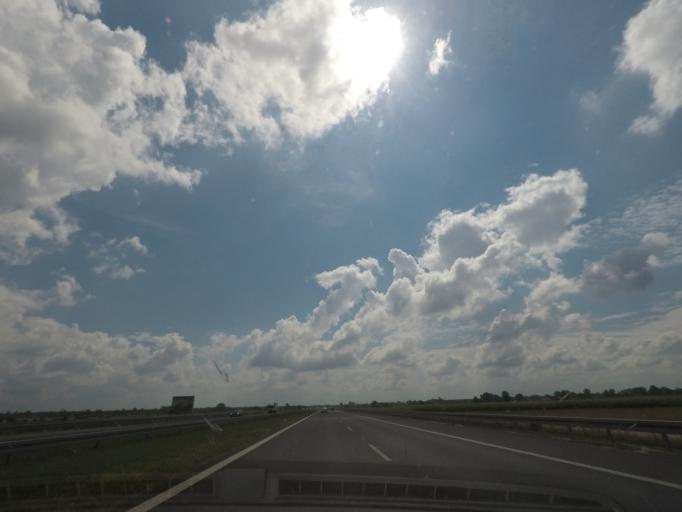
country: PL
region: Lodz Voivodeship
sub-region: Powiat zgierski
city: Strykow
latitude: 51.9706
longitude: 19.5760
